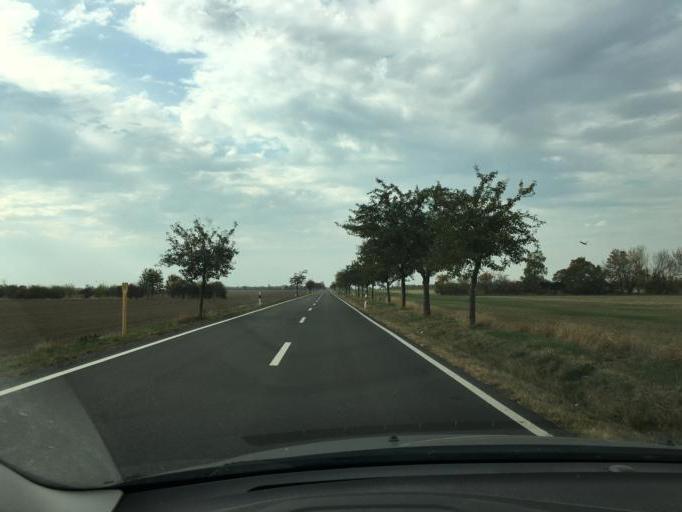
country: DE
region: Saxony
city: Wiedemar
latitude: 51.4960
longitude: 12.2226
